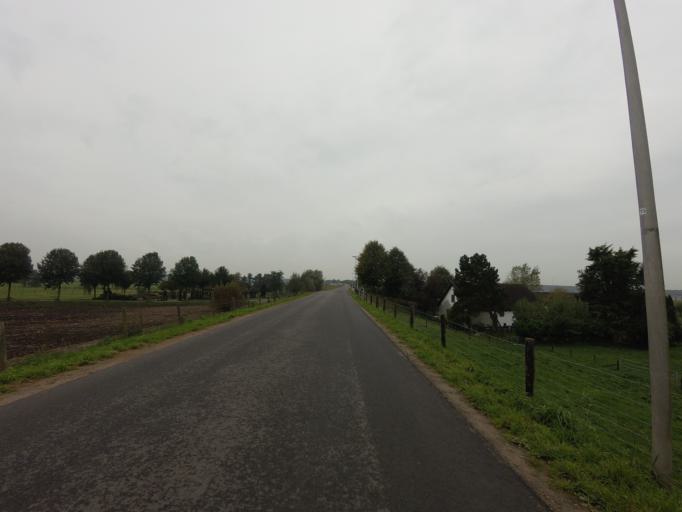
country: NL
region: Gelderland
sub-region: Gemeente Culemborg
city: Culemborg
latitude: 51.9405
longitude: 5.1569
